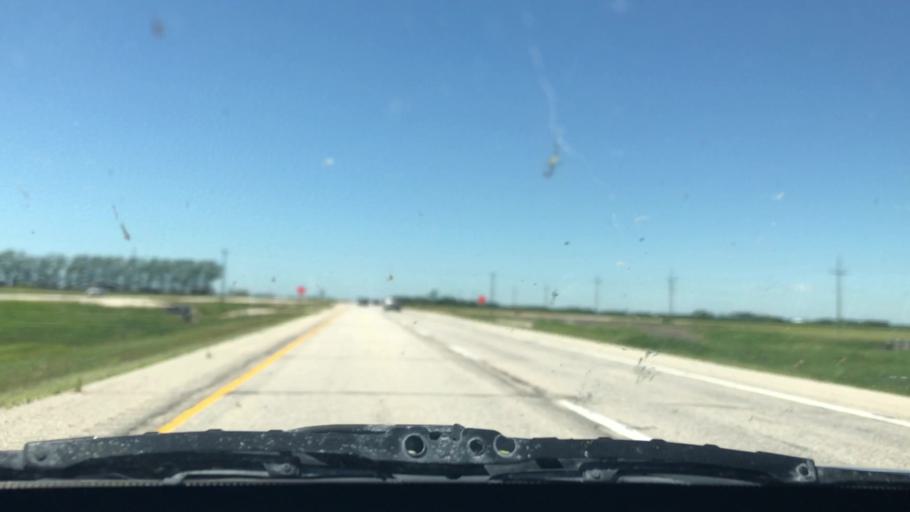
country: CA
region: Manitoba
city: Steinbach
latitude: 49.7327
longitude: -96.7250
